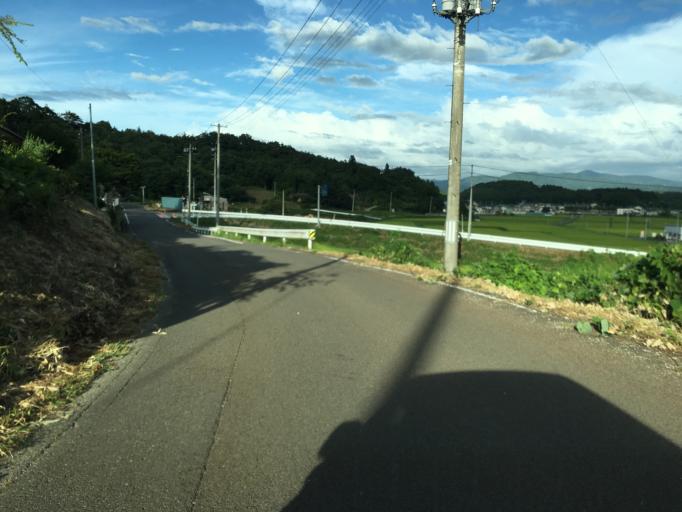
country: JP
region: Fukushima
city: Nihommatsu
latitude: 37.6338
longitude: 140.4535
